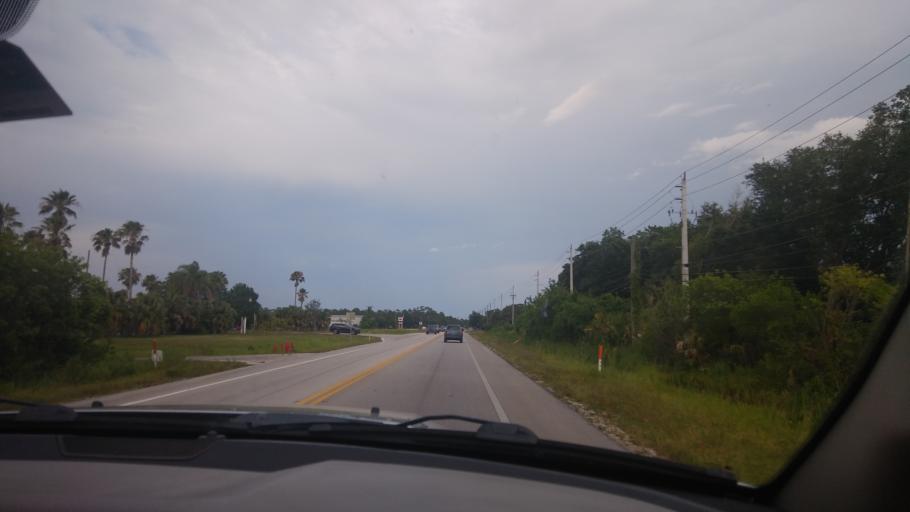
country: US
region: Florida
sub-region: Indian River County
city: Fellsmere
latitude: 27.7675
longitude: -80.5813
